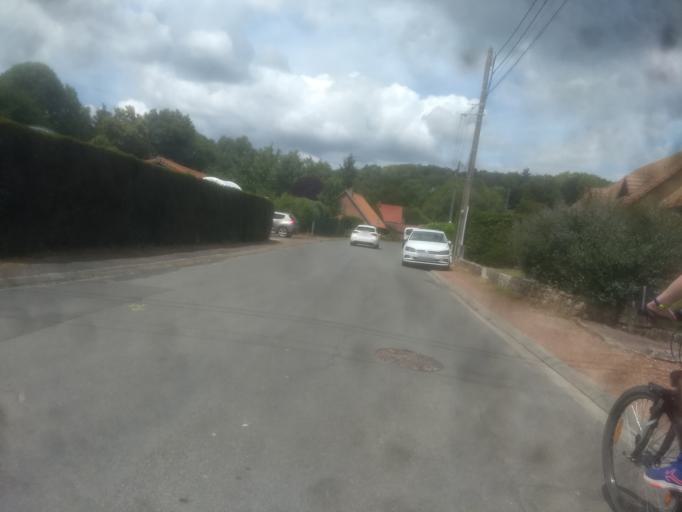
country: FR
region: Nord-Pas-de-Calais
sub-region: Departement du Pas-de-Calais
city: Mont-Saint-Eloi
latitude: 50.3378
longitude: 2.6914
